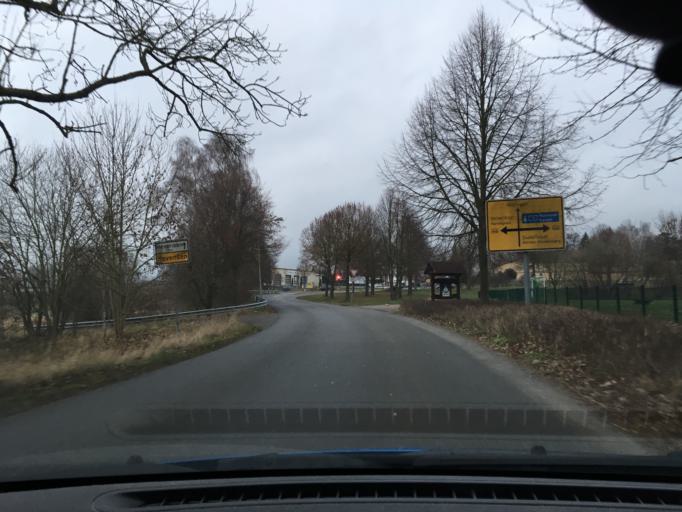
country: DE
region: Lower Saxony
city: Hardegsen
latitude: 51.6407
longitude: 9.8712
